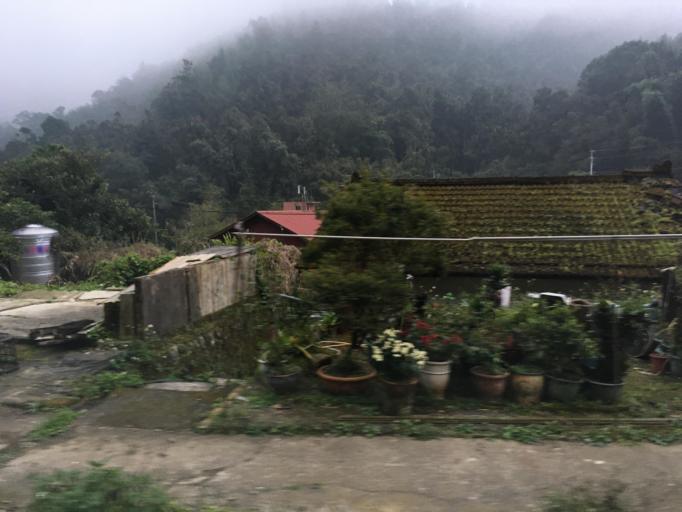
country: TW
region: Taiwan
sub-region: Chiayi
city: Jiayi Shi
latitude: 23.5043
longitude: 120.6595
